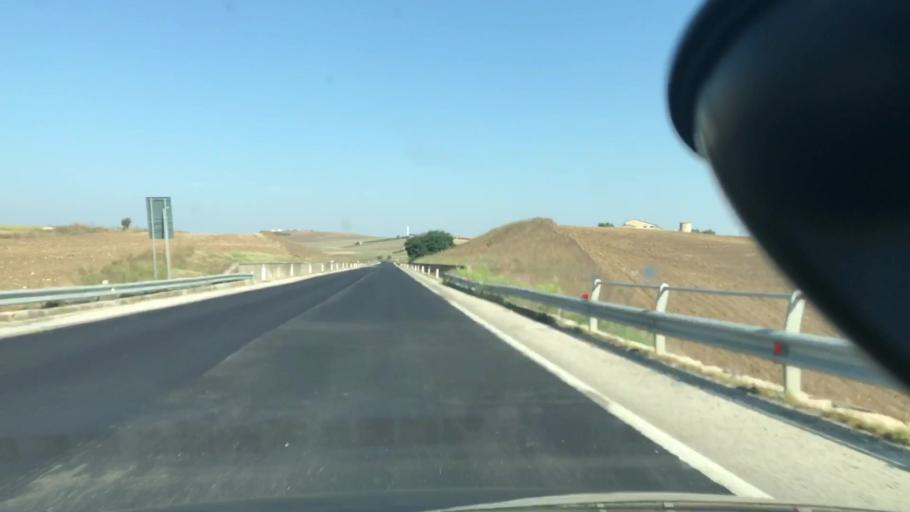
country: IT
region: Apulia
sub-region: Provincia di Barletta - Andria - Trani
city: Spinazzola
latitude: 40.9133
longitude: 16.1048
